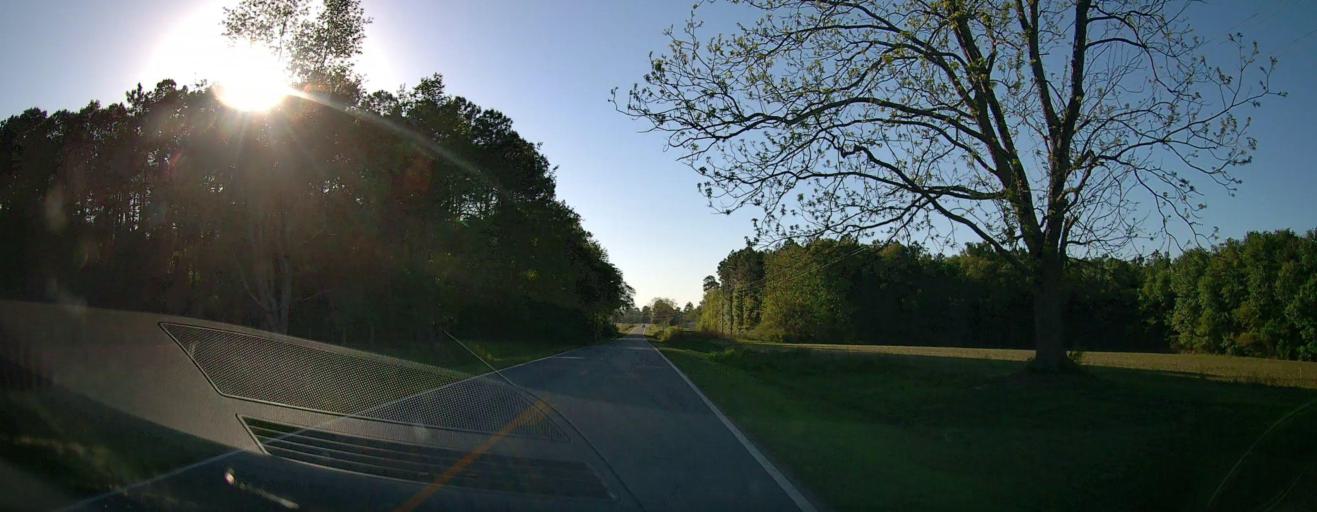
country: US
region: Georgia
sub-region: Ben Hill County
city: Fitzgerald
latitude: 31.6798
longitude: -83.1985
